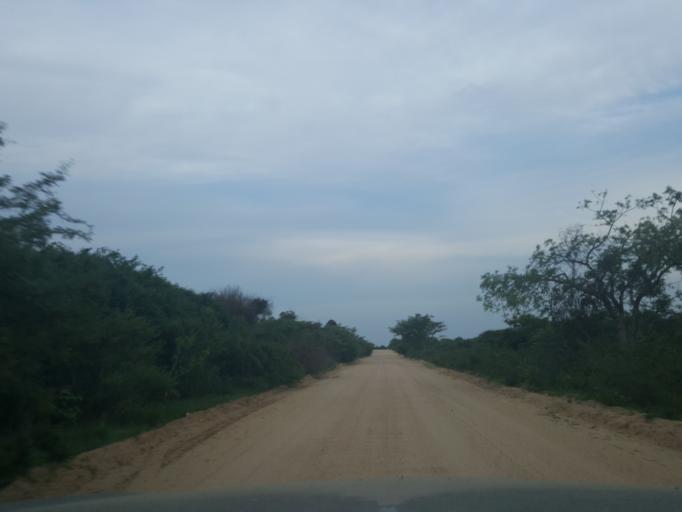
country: ZA
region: Limpopo
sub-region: Mopani District Municipality
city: Hoedspruit
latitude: -24.5654
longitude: 31.0112
